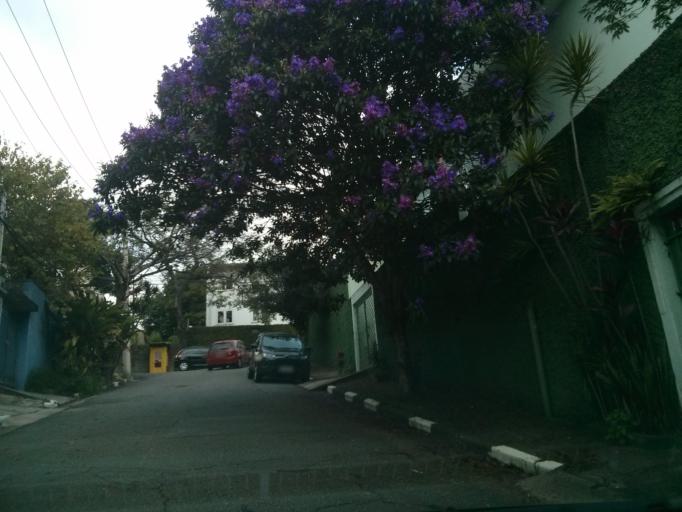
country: BR
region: Sao Paulo
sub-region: Sao Paulo
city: Sao Paulo
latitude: -23.6049
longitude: -46.6505
